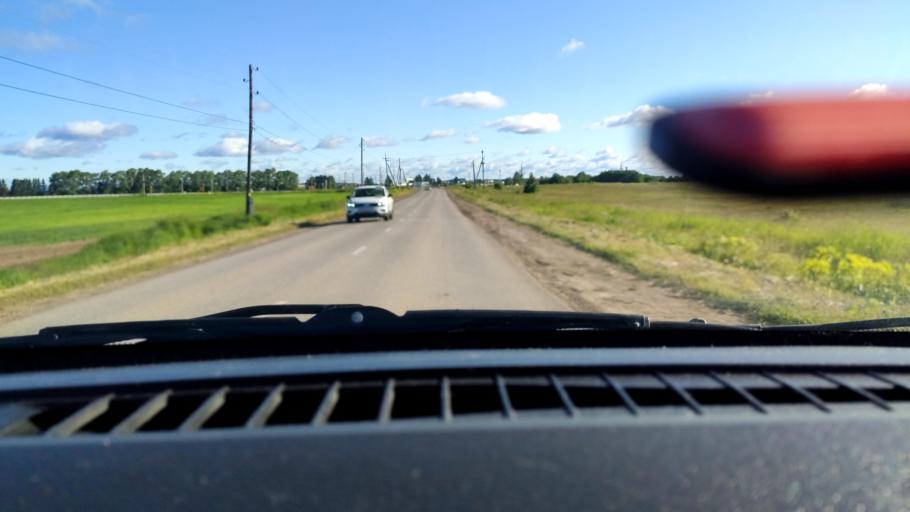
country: RU
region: Perm
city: Kultayevo
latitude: 57.8807
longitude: 55.9223
